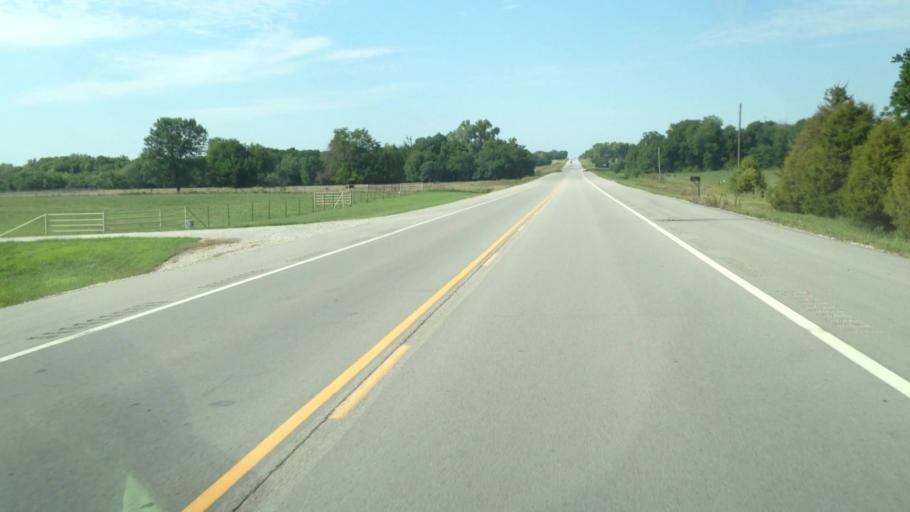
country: US
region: Kansas
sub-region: Labette County
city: Parsons
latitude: 37.2912
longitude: -95.2675
